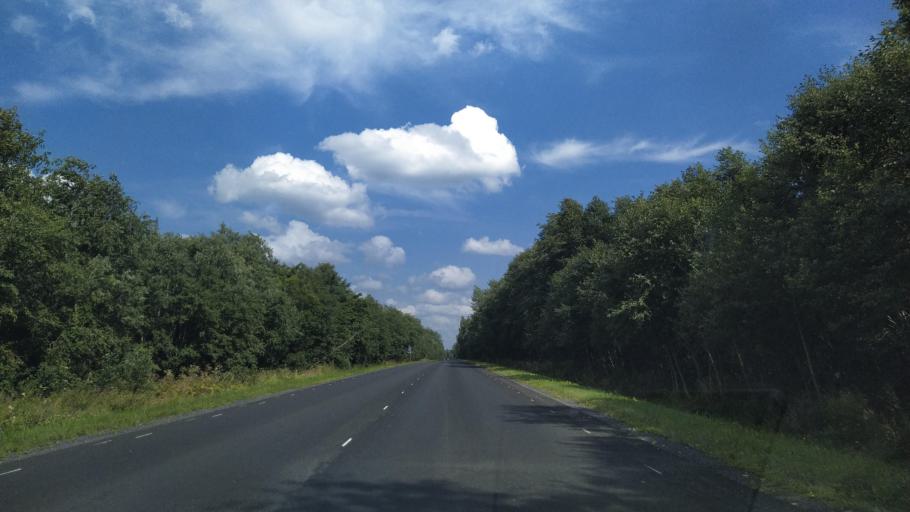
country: RU
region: Pskov
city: Porkhov
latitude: 57.7281
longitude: 29.3187
